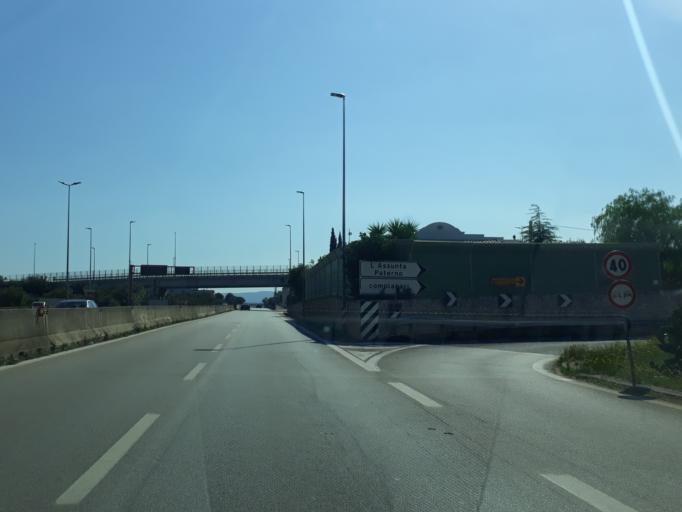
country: IT
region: Apulia
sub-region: Provincia di Brindisi
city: Fasano
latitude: 40.8815
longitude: 17.3375
